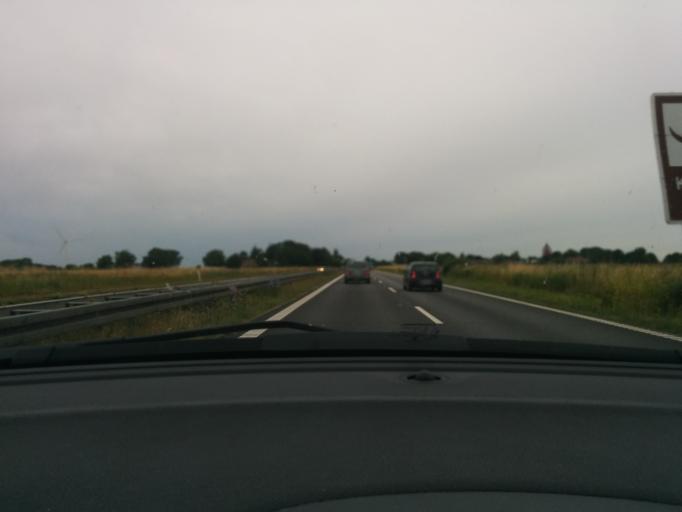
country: DK
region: Zealand
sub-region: Guldborgsund Kommune
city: Sakskobing
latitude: 54.7892
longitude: 11.5953
